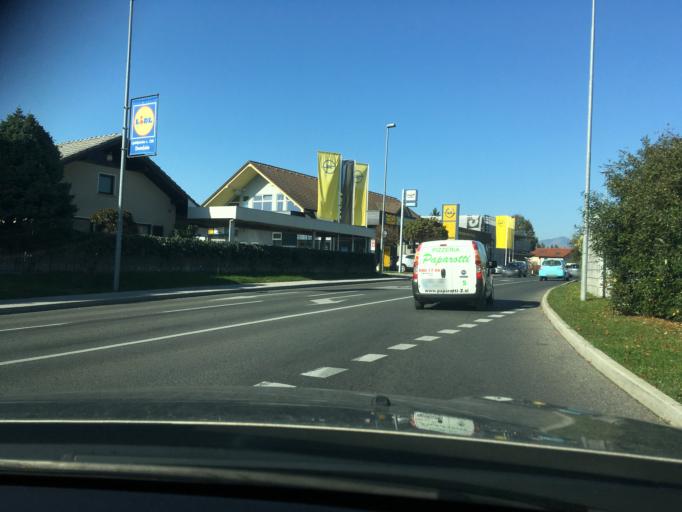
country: SI
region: Domzale
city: Domzale
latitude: 46.1455
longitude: 14.5936
